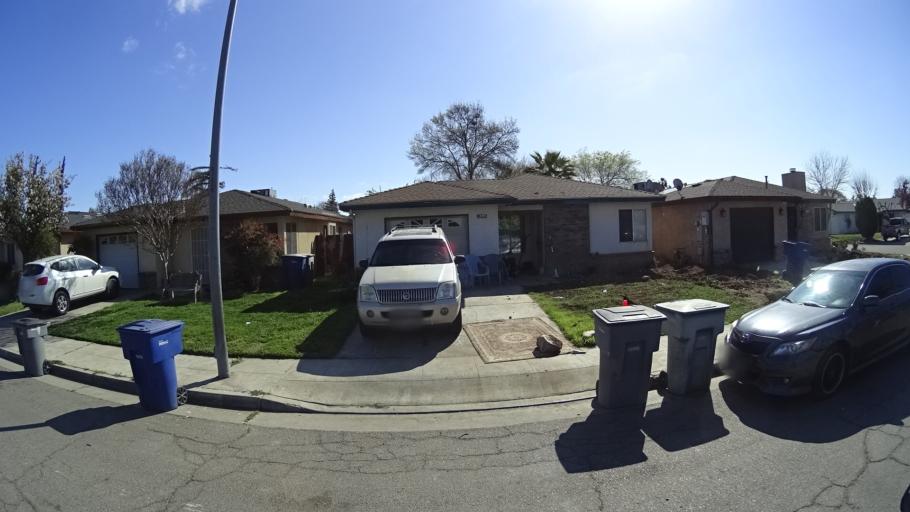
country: US
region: California
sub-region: Fresno County
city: West Park
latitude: 36.7985
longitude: -119.8872
